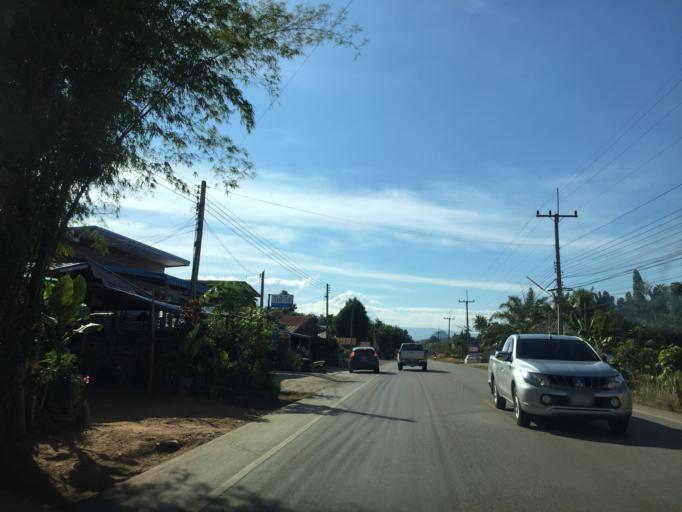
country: TH
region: Loei
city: Wang Saphung
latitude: 17.3154
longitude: 101.7500
